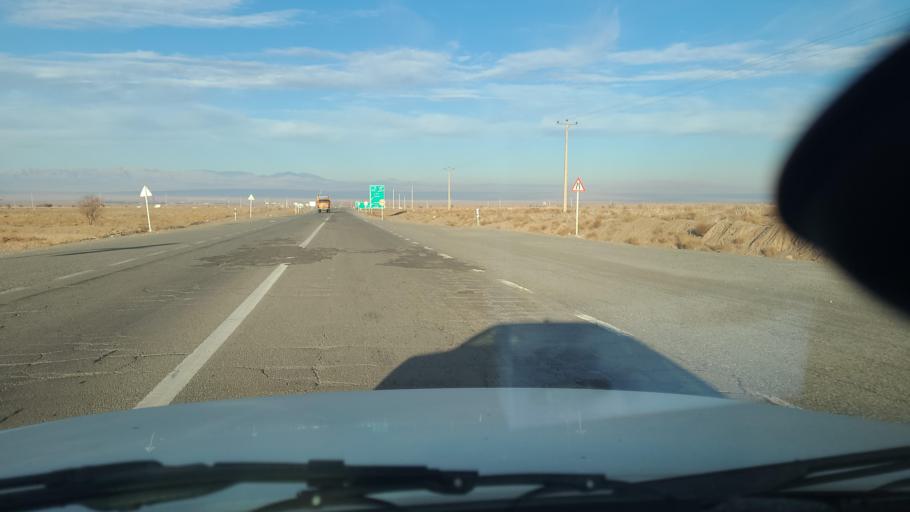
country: IR
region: Razavi Khorasan
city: Neqab
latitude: 36.5084
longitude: 57.5369
